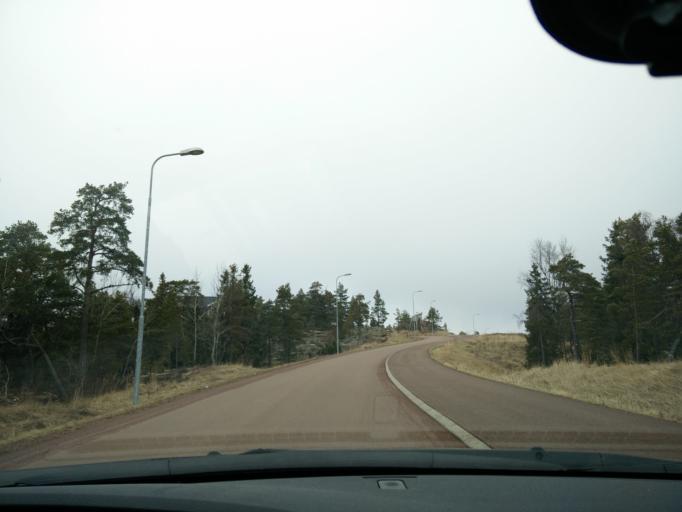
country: AX
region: Alands landsbygd
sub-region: Jomala
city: Jomala
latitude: 60.1288
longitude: 19.9284
